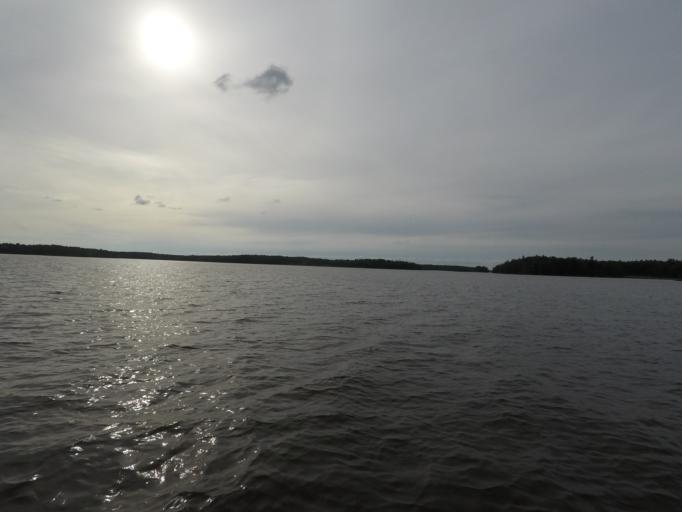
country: SE
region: Soedermanland
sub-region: Eskilstuna Kommun
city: Torshalla
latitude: 59.4716
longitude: 16.4390
